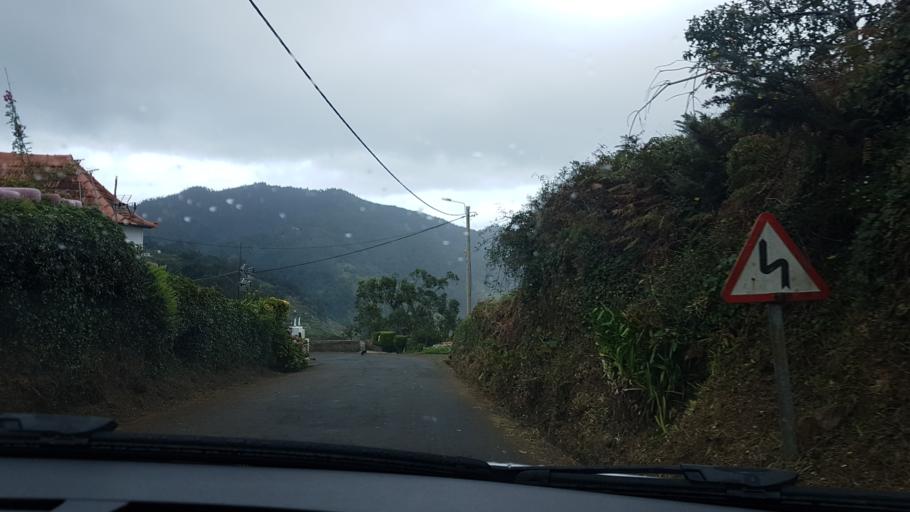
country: PT
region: Madeira
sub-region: Santa Cruz
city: Santa Cruz
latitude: 32.7301
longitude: -16.8081
